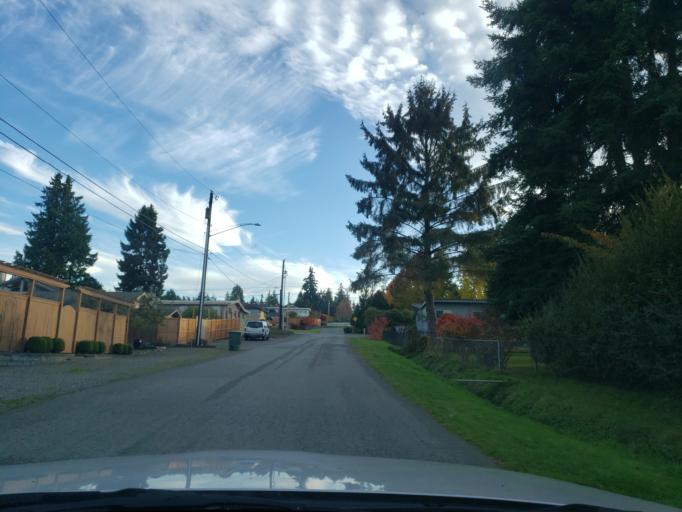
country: US
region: Washington
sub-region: Snohomish County
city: Edmonds
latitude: 47.8155
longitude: -122.3643
